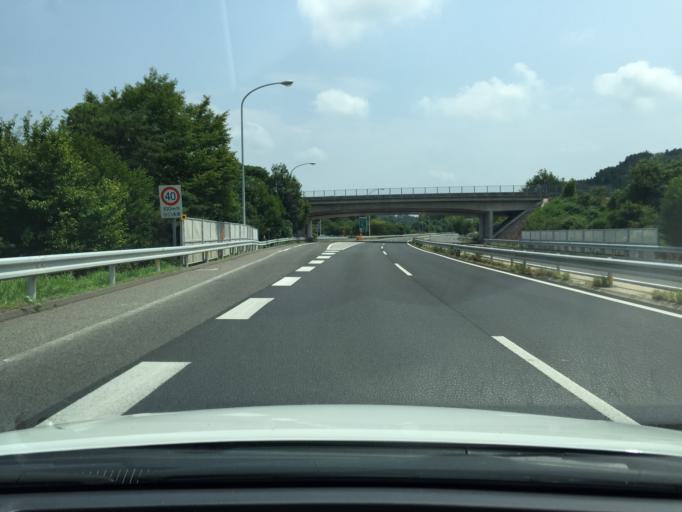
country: JP
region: Fukushima
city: Miharu
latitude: 37.4429
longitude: 140.4392
